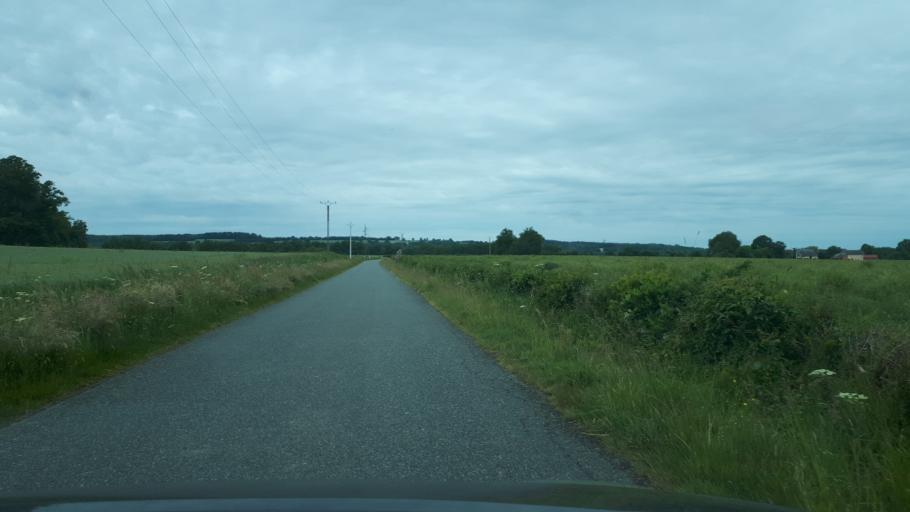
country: FR
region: Centre
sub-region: Departement du Cher
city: Henrichemont
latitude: 47.4042
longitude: 2.6445
